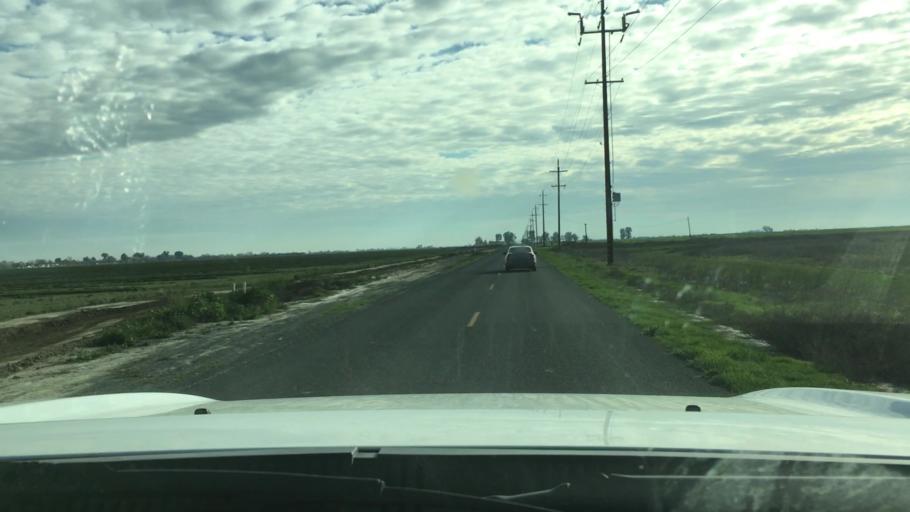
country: US
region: California
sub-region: Kings County
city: Stratford
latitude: 36.2259
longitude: -119.7784
